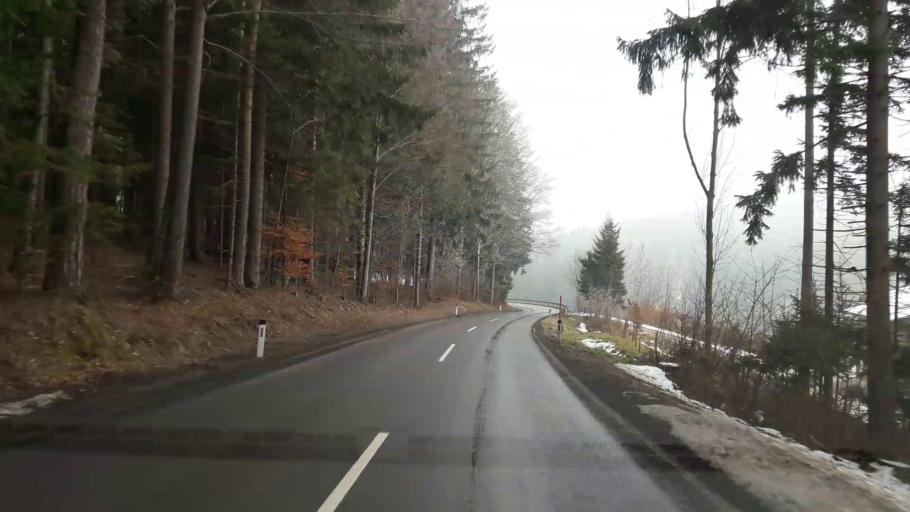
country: AT
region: Lower Austria
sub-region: Politischer Bezirk Neunkirchen
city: Sankt Corona am Wechsel
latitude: 47.5733
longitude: 16.0309
